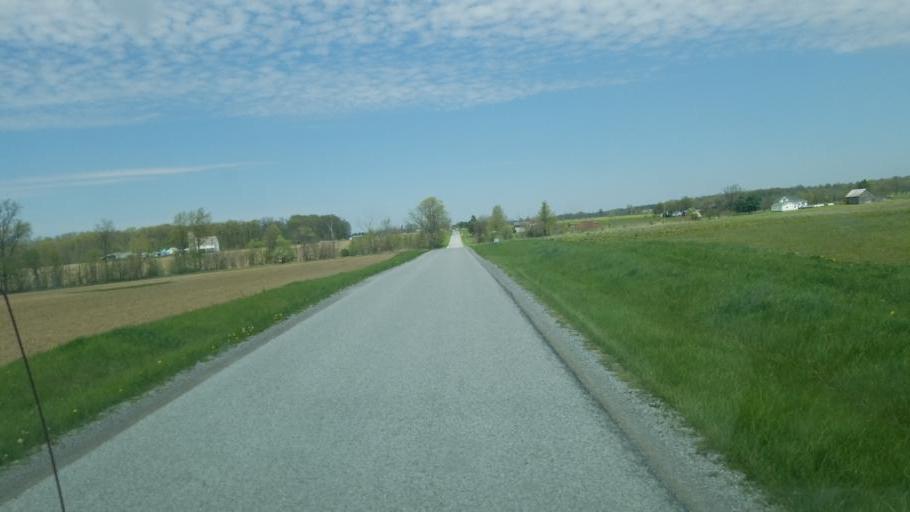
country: US
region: Ohio
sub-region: Hardin County
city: Ada
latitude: 40.8069
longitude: -83.8990
